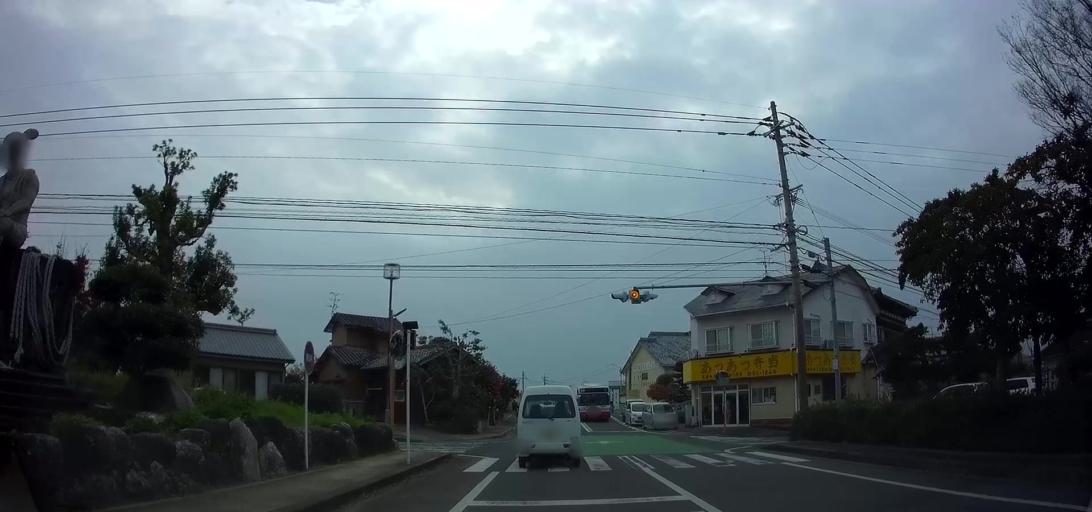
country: JP
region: Nagasaki
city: Shimabara
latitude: 32.6592
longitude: 130.2976
